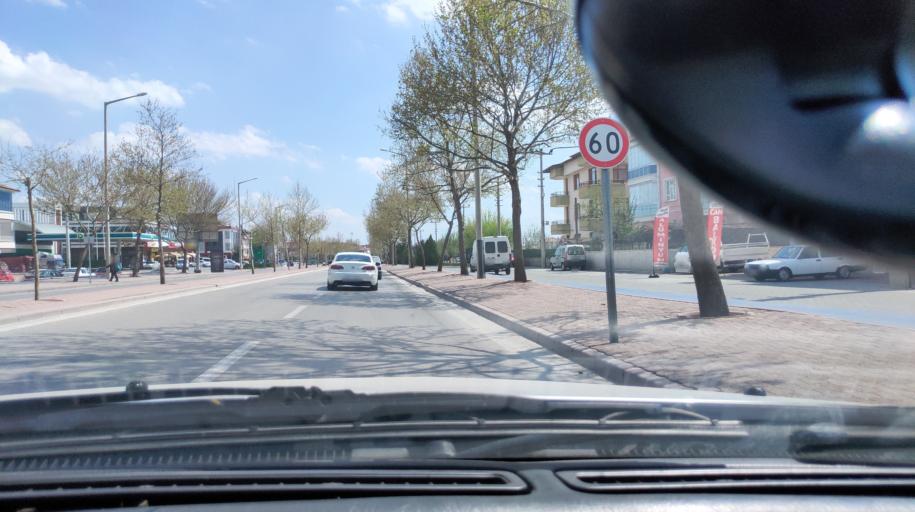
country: TR
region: Konya
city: Selcuklu
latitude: 37.9289
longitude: 32.4938
